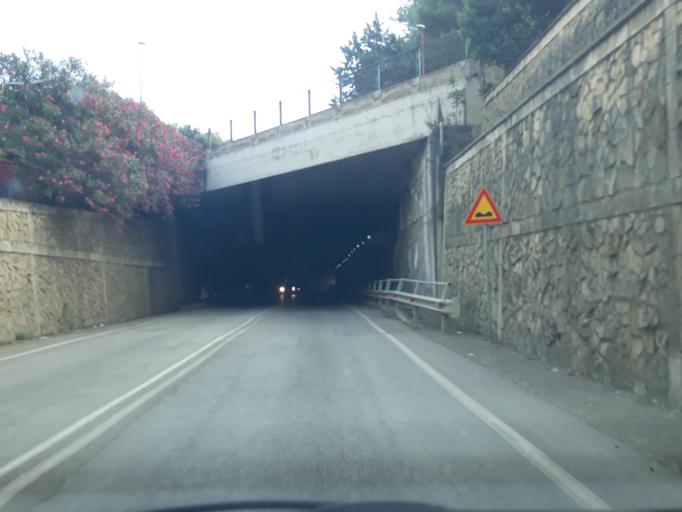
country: IT
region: Sicily
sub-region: Palermo
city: Cefalu
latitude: 38.0329
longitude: 14.0265
